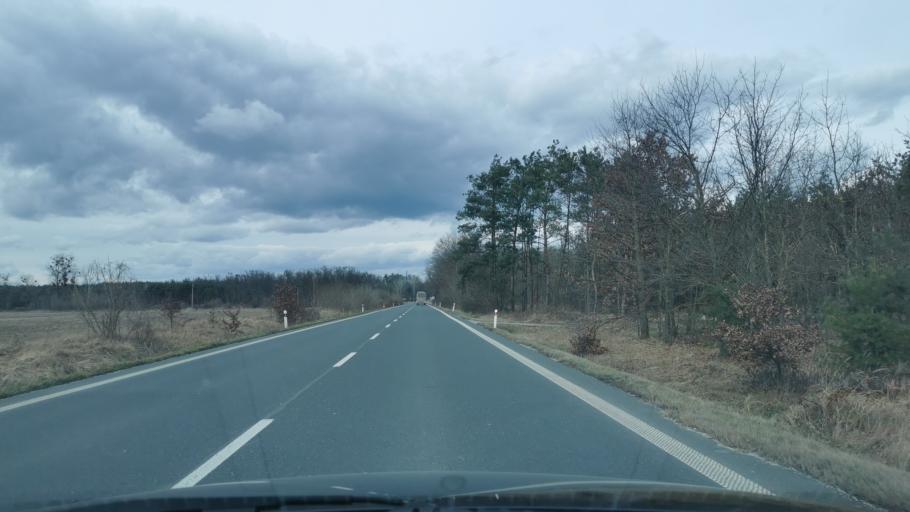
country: CZ
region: South Moravian
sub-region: Okres Breclav
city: Lanzhot
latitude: 48.6962
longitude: 17.0384
